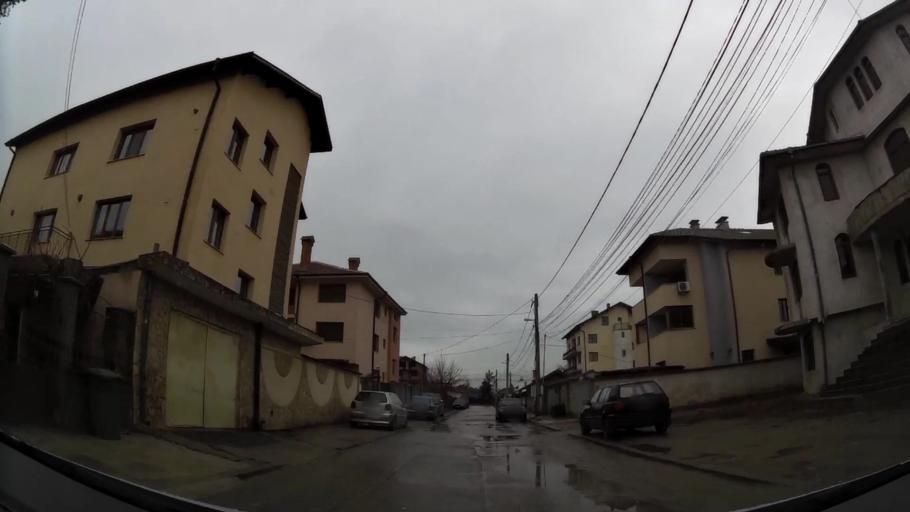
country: BG
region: Sofia-Capital
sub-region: Stolichna Obshtina
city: Sofia
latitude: 42.6236
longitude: 23.4068
